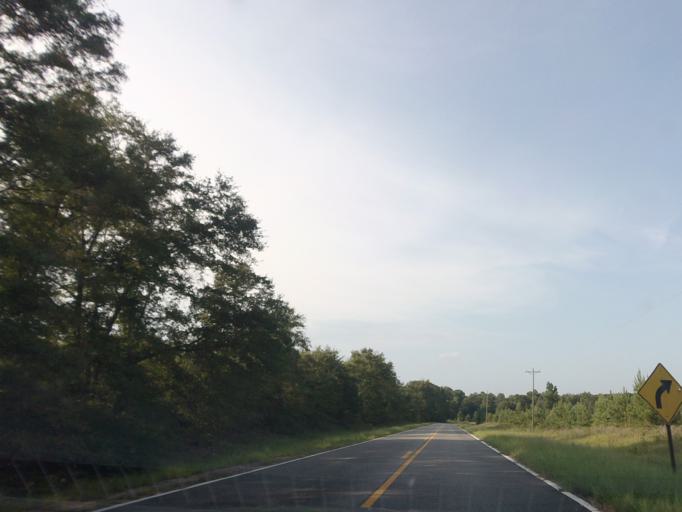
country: US
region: Georgia
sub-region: Bleckley County
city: Cochran
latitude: 32.4921
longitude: -83.3024
